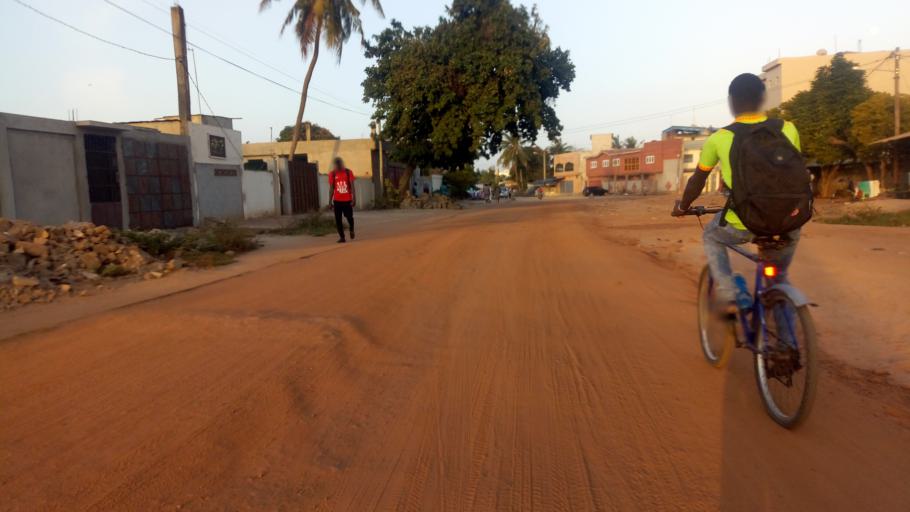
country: TG
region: Maritime
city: Lome
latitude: 6.1928
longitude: 1.1972
